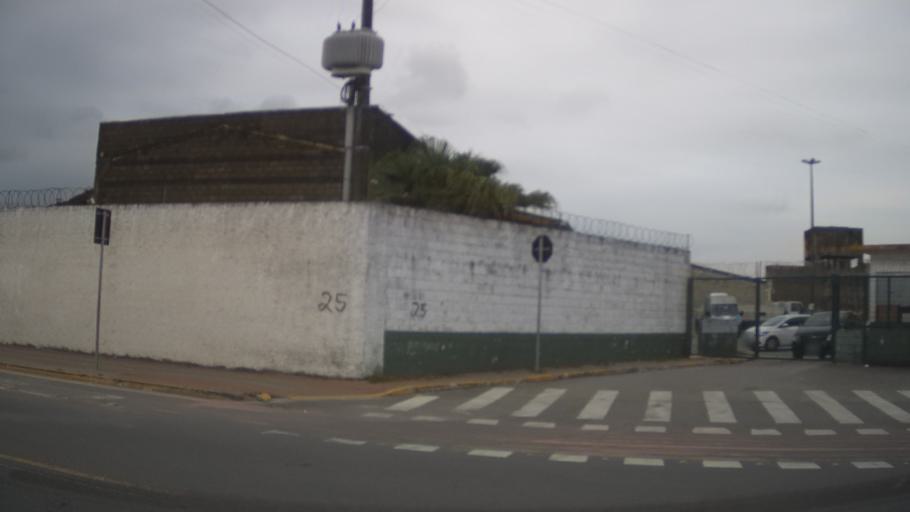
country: BR
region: Sao Paulo
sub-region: Praia Grande
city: Praia Grande
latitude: -24.0076
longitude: -46.4478
